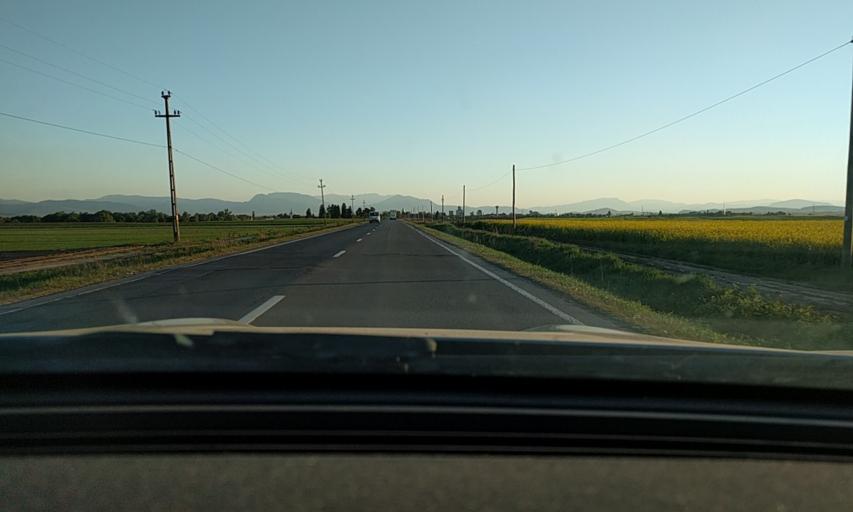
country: RO
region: Covasna
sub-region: Comuna Ozun
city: Ozun
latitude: 45.8112
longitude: 25.8621
